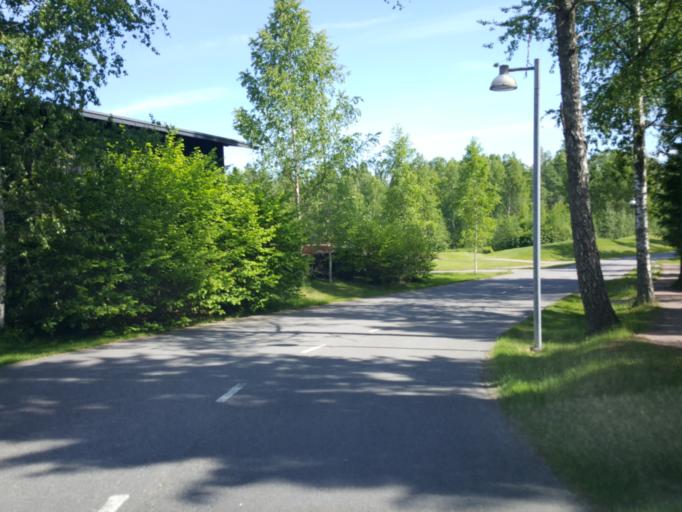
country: FI
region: Uusimaa
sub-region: Helsinki
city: Kirkkonummi
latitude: 60.1205
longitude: 24.5254
